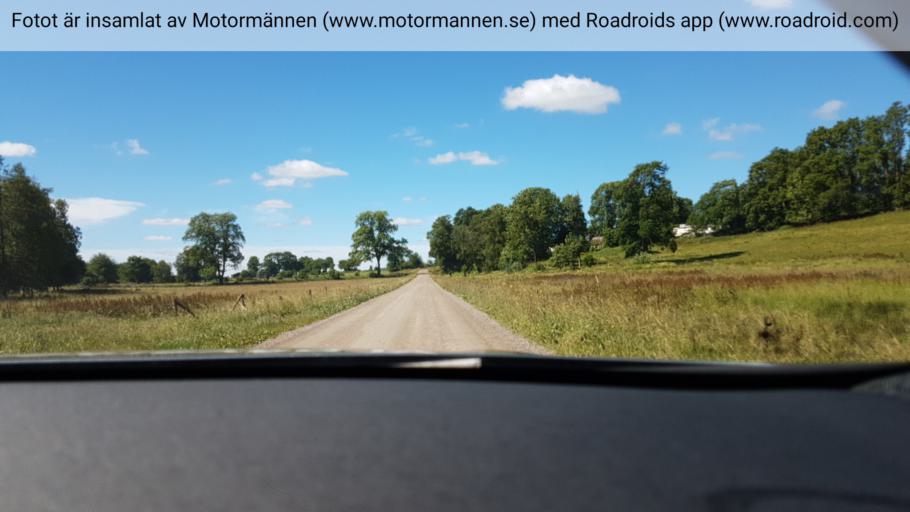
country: SE
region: Vaestra Goetaland
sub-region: Falkopings Kommun
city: Akarp
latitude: 58.2043
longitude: 13.7422
